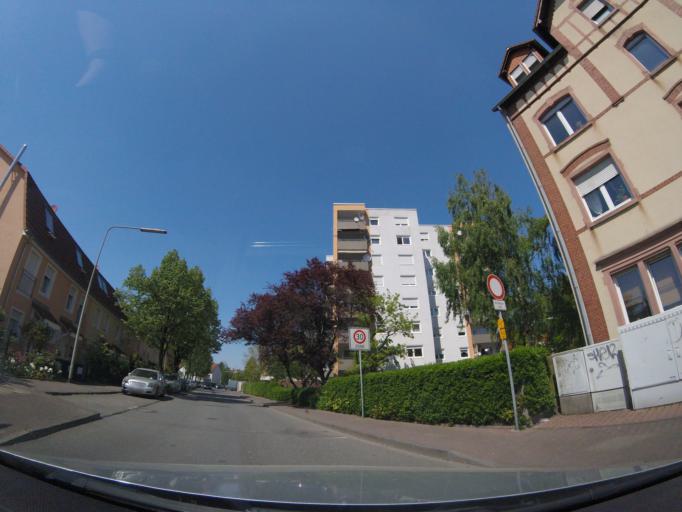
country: DE
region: Hesse
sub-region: Regierungsbezirk Darmstadt
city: Offenbach
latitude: 50.1320
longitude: 8.7587
